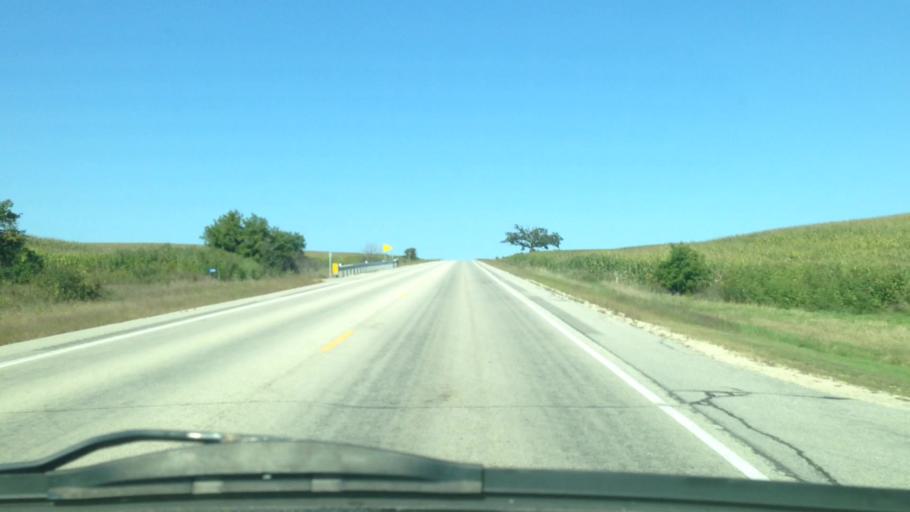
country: US
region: Minnesota
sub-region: Fillmore County
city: Rushford
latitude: 43.8521
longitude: -91.7484
